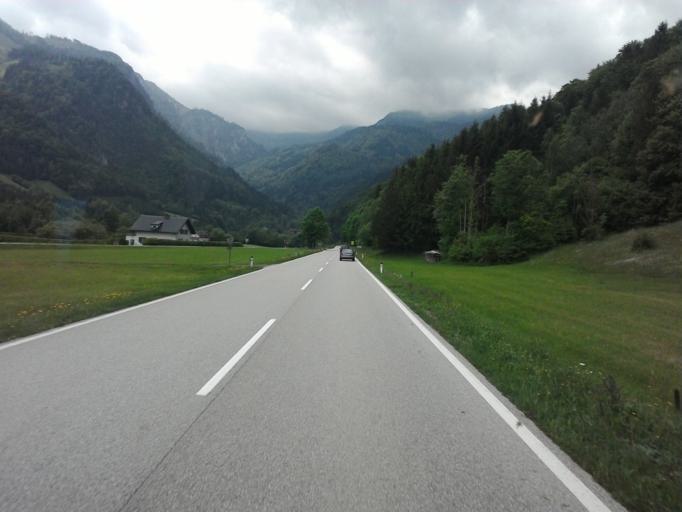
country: AT
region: Upper Austria
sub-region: Politischer Bezirk Steyr-Land
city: Weyer
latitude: 47.8559
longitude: 14.6273
